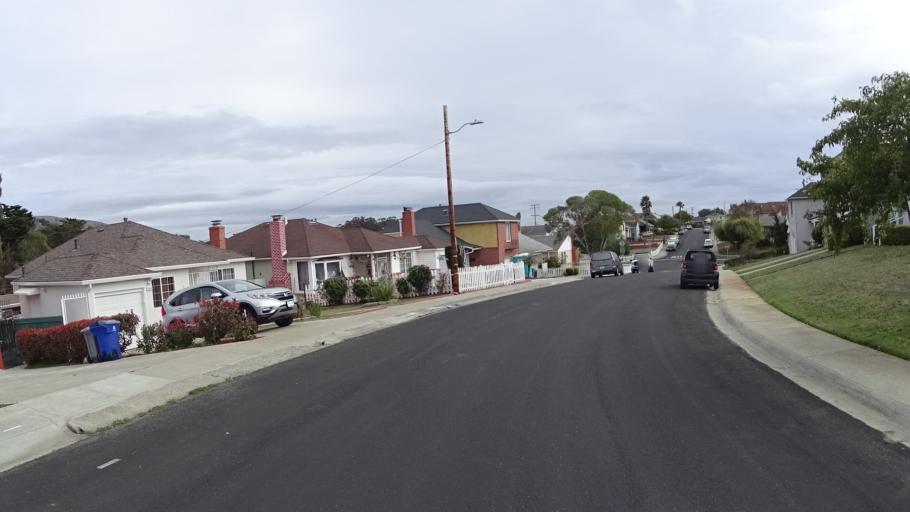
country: US
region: California
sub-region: San Mateo County
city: South San Francisco
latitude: 37.6525
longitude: -122.4345
